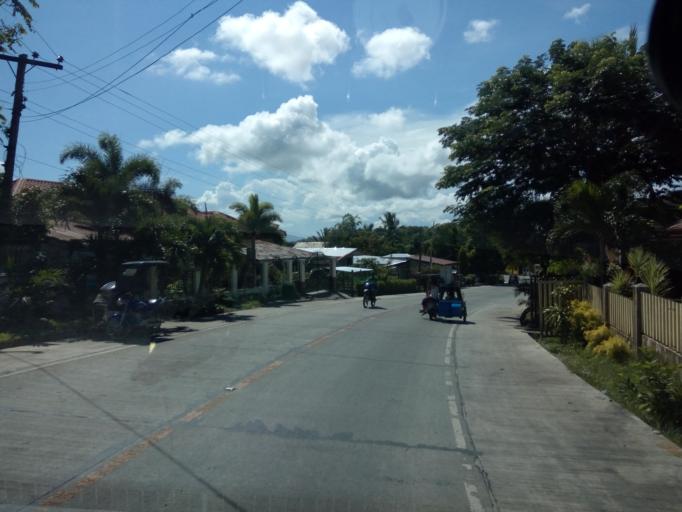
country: PH
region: Central Luzon
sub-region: Province of Nueva Ecija
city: Pantabangan
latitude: 15.8050
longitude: 121.1475
